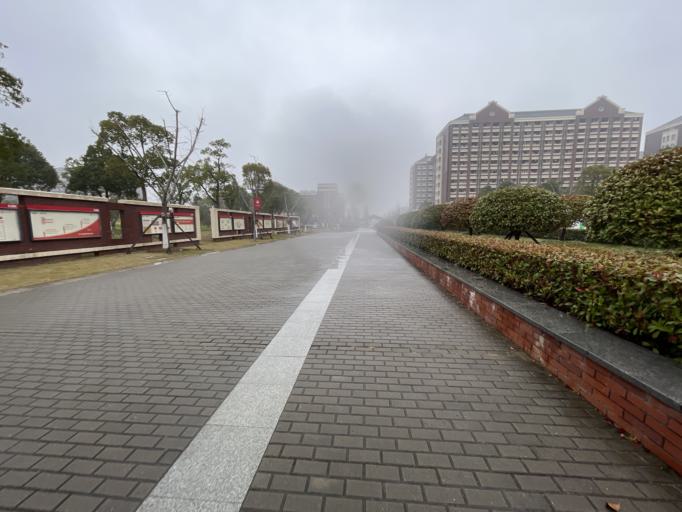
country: CN
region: Shanghai Shi
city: Shuyuan
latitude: 30.8948
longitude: 121.8880
